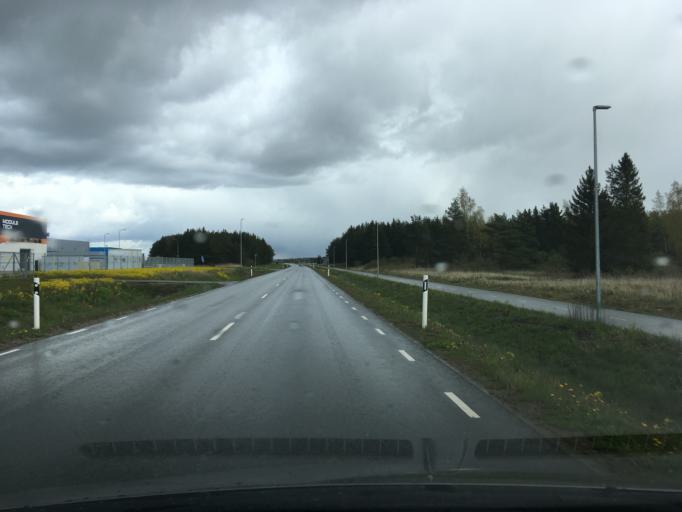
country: EE
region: Harju
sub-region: Joelaehtme vald
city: Loo
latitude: 59.4459
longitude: 24.9420
